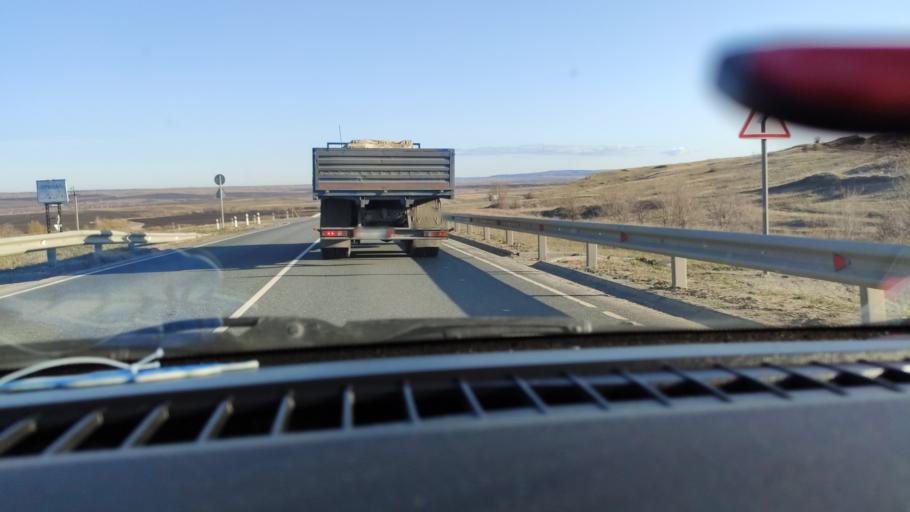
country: RU
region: Saratov
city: Alekseyevka
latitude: 52.3252
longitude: 47.9204
